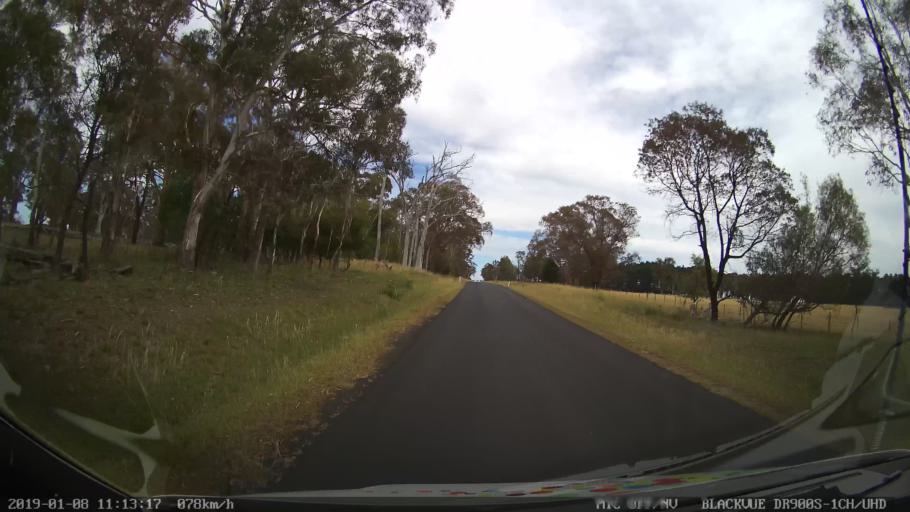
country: AU
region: New South Wales
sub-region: Guyra
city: Guyra
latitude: -30.2300
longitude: 151.6026
